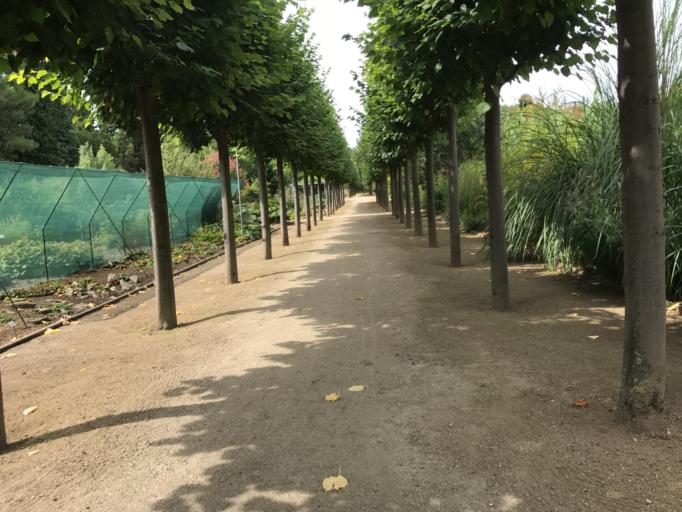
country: DE
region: Rheinland-Pfalz
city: Mainz
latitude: 49.9910
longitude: 8.2425
